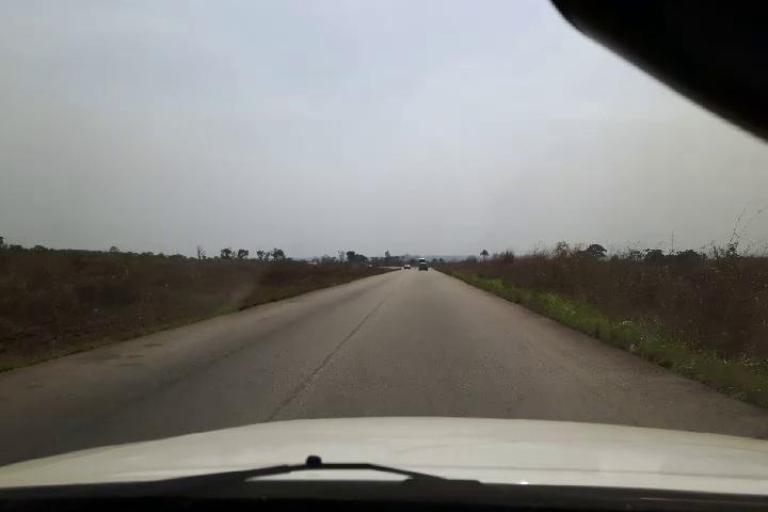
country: SL
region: Northern Province
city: Yonibana
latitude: 8.3790
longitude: -12.2030
